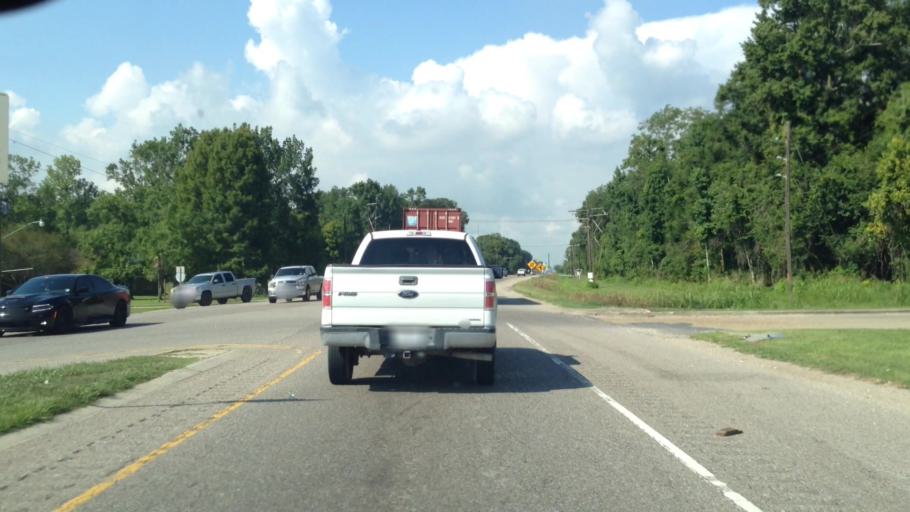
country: US
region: Louisiana
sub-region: Ascension Parish
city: Sorrento
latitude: 30.1699
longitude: -90.8785
